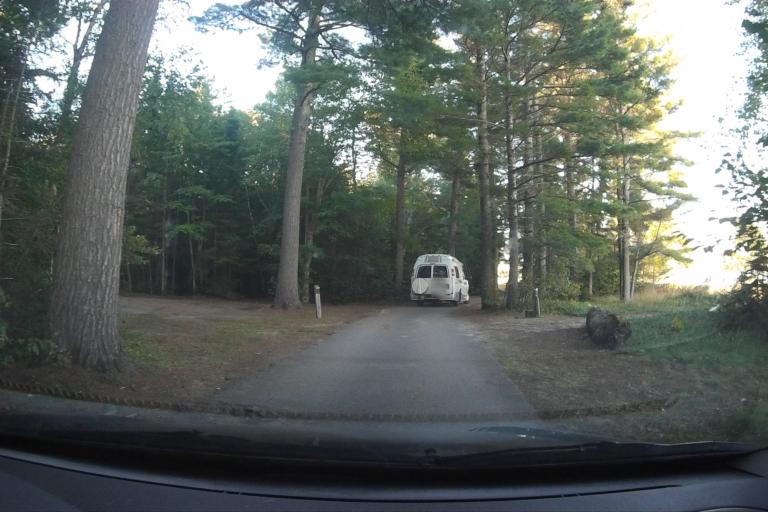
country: CA
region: Ontario
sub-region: Algoma
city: Sault Ste. Marie
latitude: 46.9693
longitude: -84.6940
